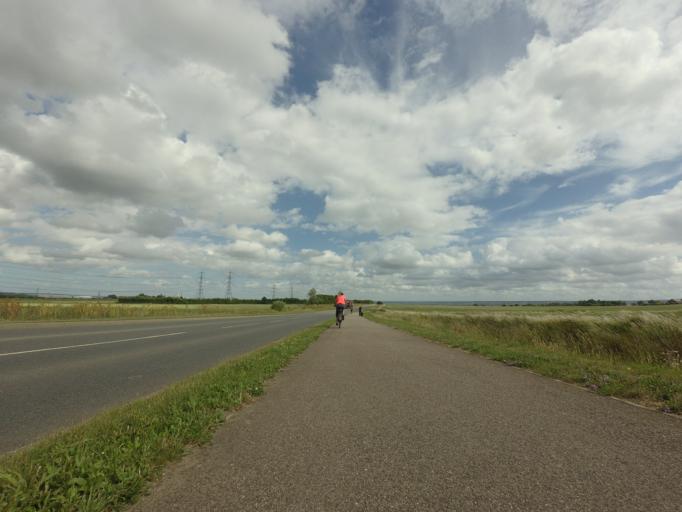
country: GB
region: England
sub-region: Kent
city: Hoo
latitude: 51.4336
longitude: 0.5705
